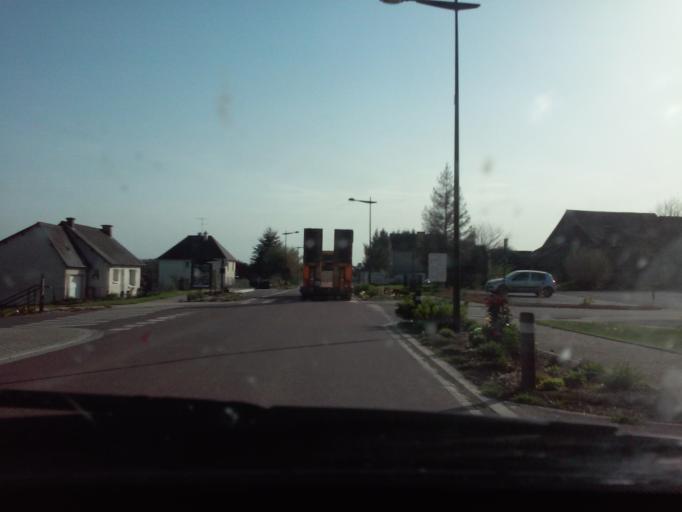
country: FR
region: Brittany
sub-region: Departement d'Ille-et-Vilaine
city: Saint-Jean-sur-Couesnon
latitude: 48.2895
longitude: -1.3702
